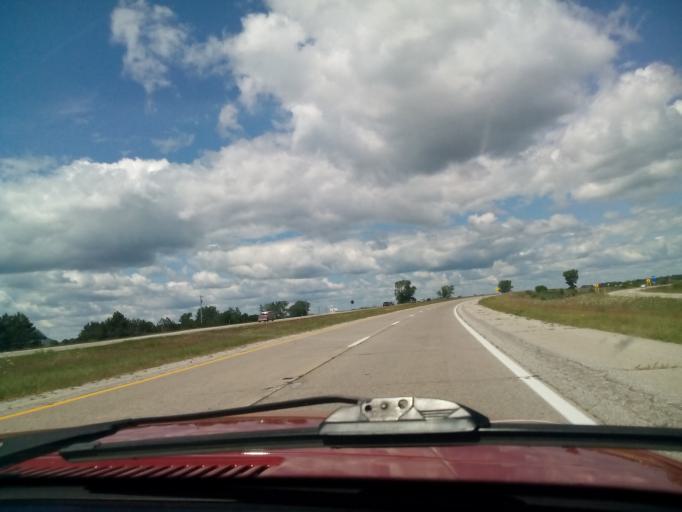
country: US
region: Michigan
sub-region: Bay County
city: Auburn
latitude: 43.6637
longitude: -84.0089
